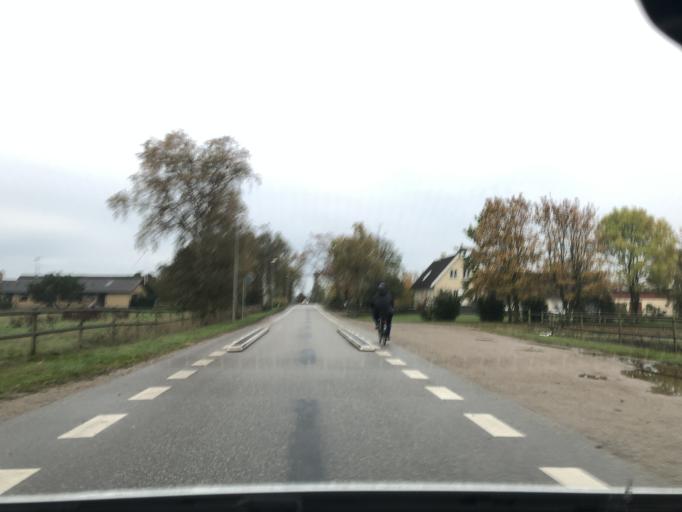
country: DK
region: Capital Region
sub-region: Tarnby Kommune
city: Tarnby
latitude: 55.5805
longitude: 12.6006
